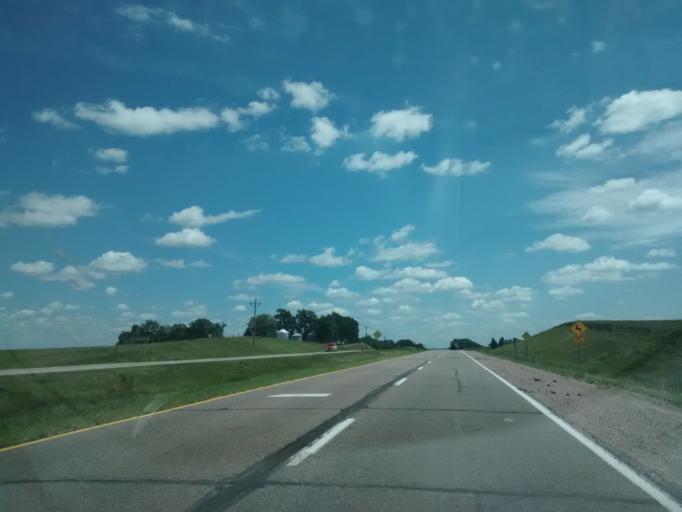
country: US
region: Iowa
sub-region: Woodbury County
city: Moville
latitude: 42.4748
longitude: -96.1347
